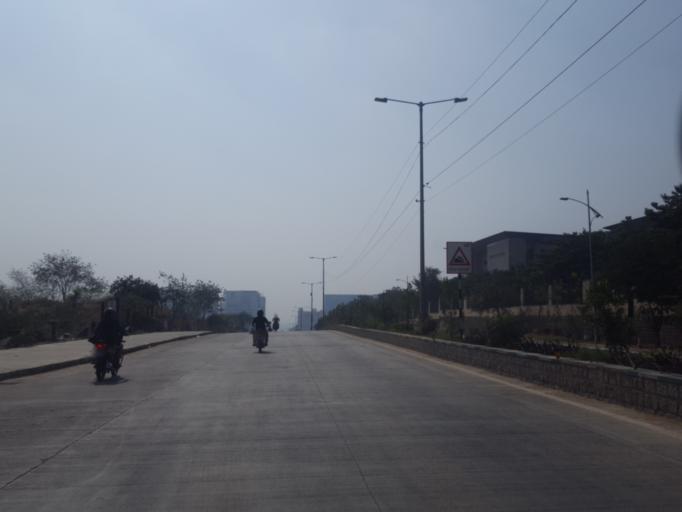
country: IN
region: Telangana
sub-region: Medak
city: Serilingampalle
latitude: 17.4322
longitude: 78.3447
